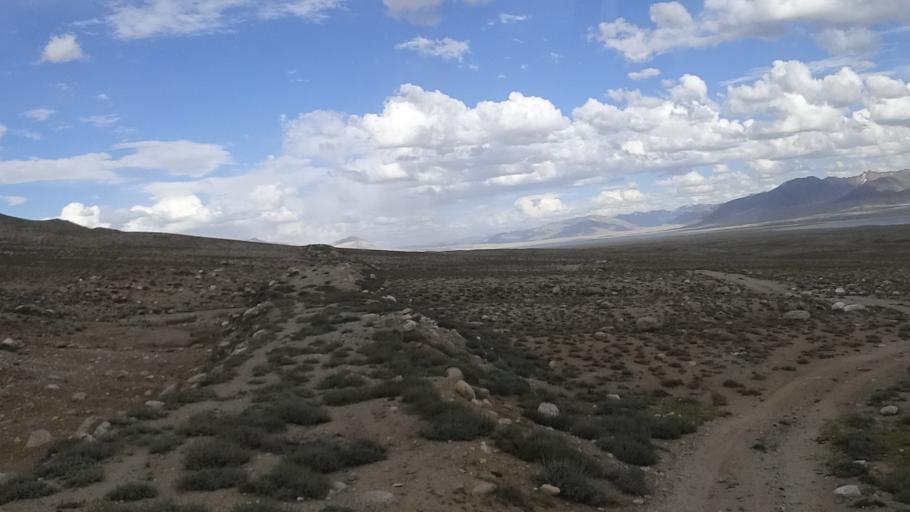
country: TJ
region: Gorno-Badakhshan
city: Murghob
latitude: 37.4686
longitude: 73.5804
